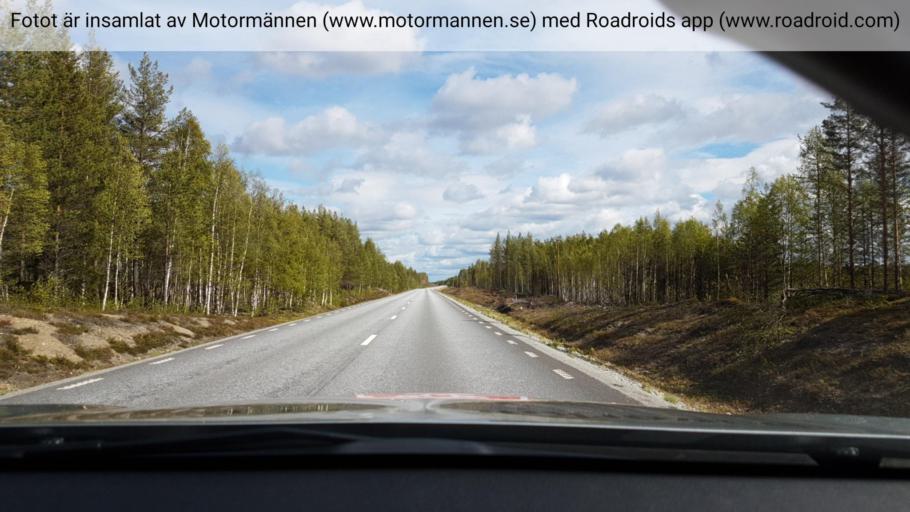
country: SE
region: Vaesternorrland
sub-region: OErnskoeldsviks Kommun
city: Bredbyn
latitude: 64.1006
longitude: 18.1607
